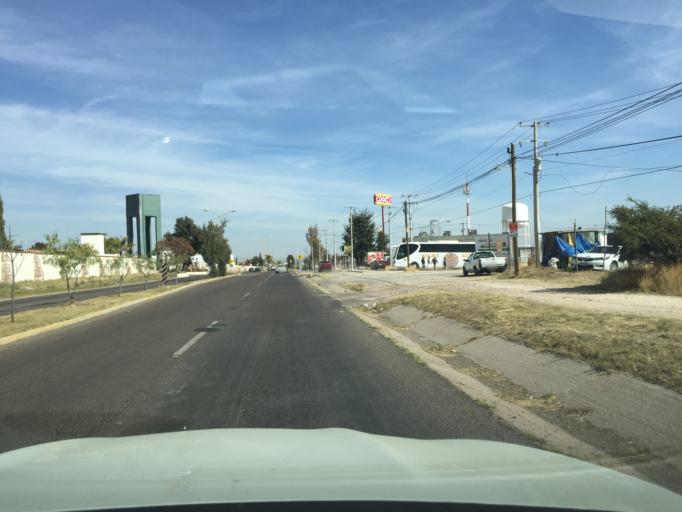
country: MX
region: Aguascalientes
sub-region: Aguascalientes
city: La Loma de los Negritos
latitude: 21.8575
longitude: -102.3467
